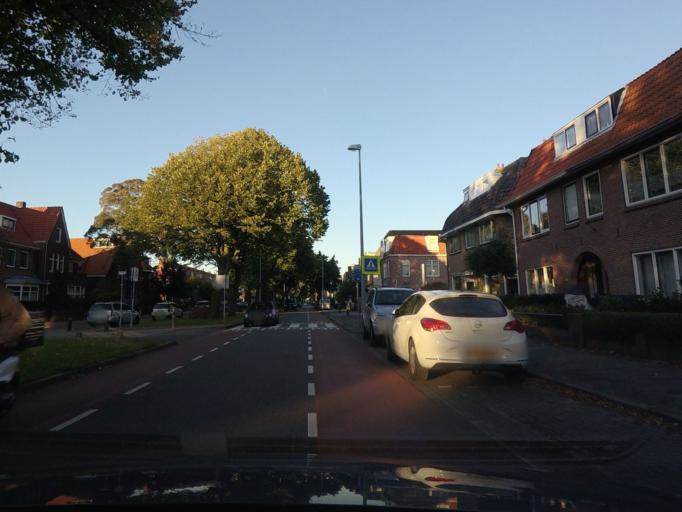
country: NL
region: North Holland
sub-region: Gemeente Alkmaar
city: Alkmaar
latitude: 52.6313
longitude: 4.7334
